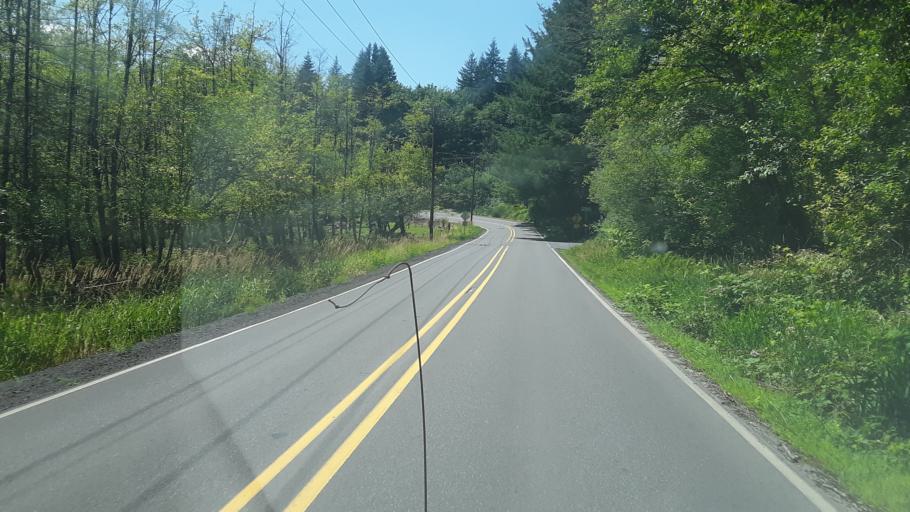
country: US
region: Washington
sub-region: Clark County
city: Amboy
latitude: 45.8956
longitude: -122.4792
